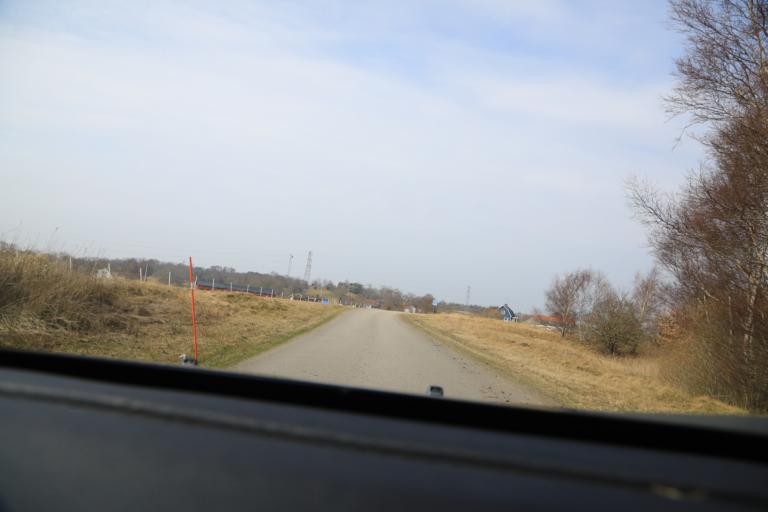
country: SE
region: Halland
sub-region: Kungsbacka Kommun
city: Frillesas
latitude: 57.2669
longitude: 12.1610
